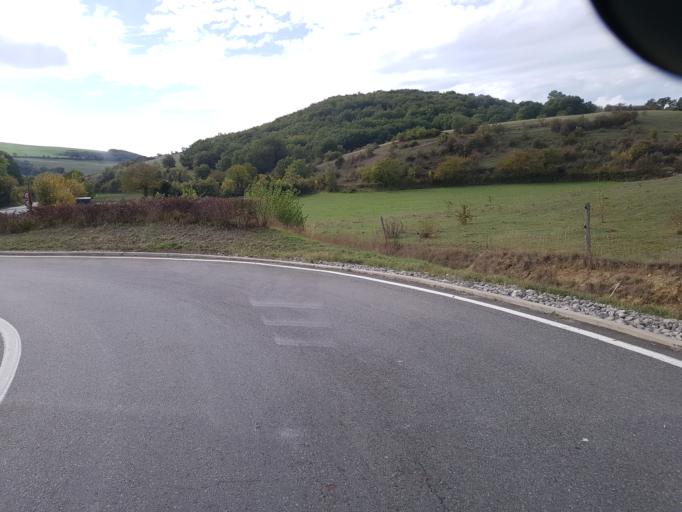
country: FR
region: Midi-Pyrenees
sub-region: Departement de l'Aveyron
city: Saint-Affrique
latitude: 43.9848
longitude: 2.9331
